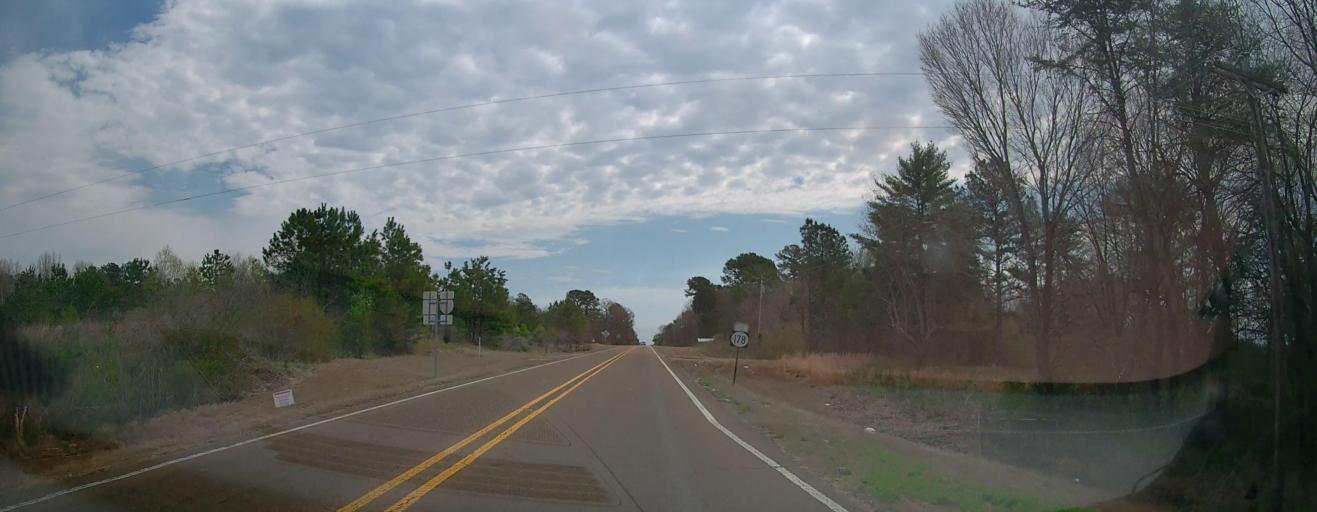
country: US
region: Mississippi
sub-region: Marshall County
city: Holly Springs
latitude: 34.8278
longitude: -89.5638
